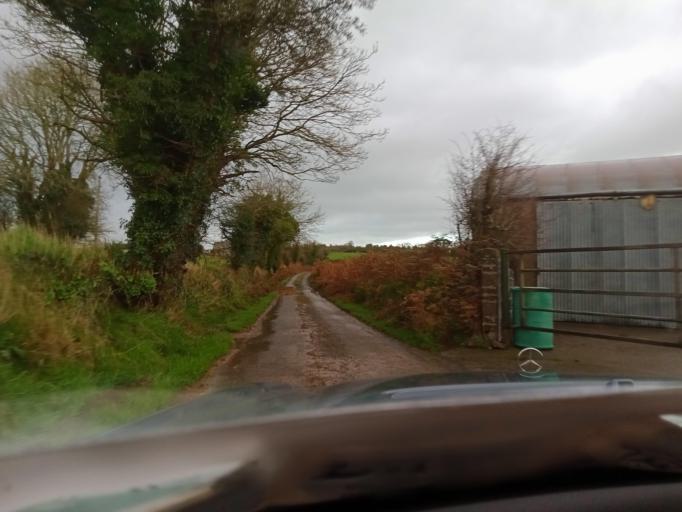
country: IE
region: Leinster
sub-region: Kilkenny
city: Mooncoin
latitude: 52.2605
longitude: -7.2028
